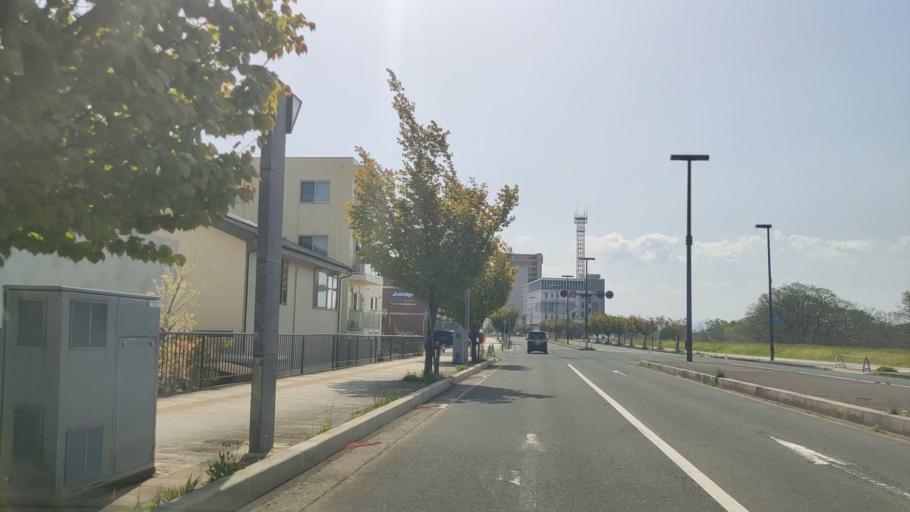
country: JP
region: Iwate
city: Morioka-shi
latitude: 39.7026
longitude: 141.1265
